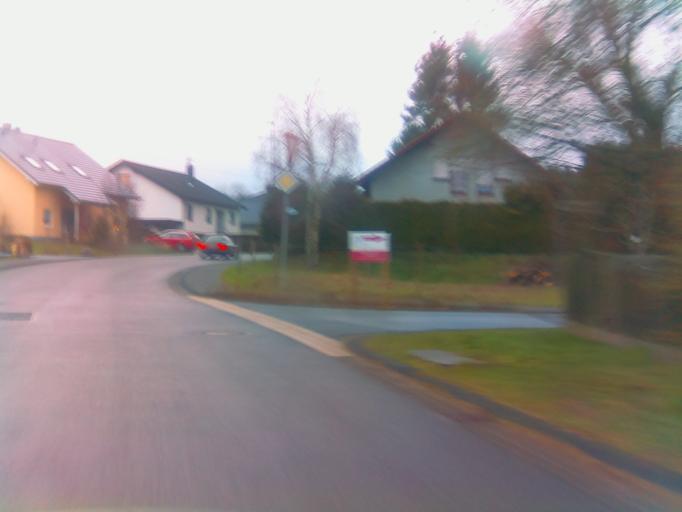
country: DE
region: Rheinland-Pfalz
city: Brucken
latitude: 49.6335
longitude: 7.1130
